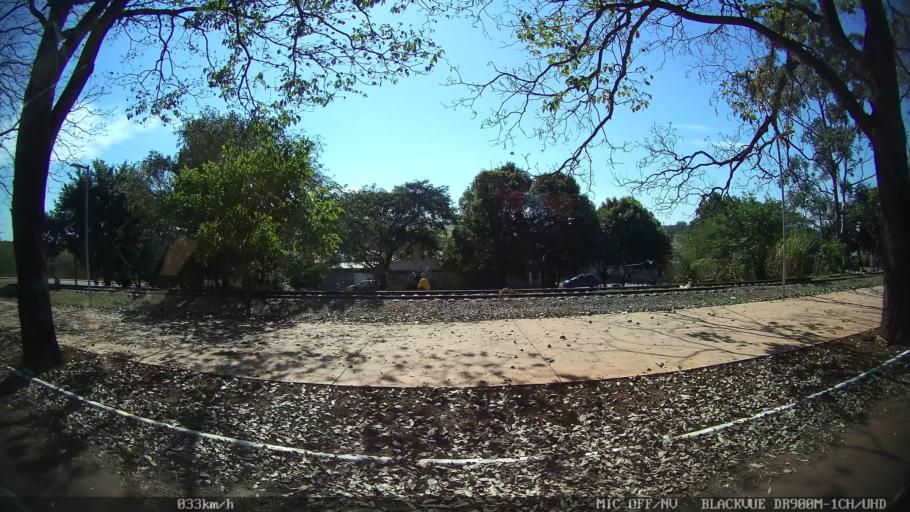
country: BR
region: Sao Paulo
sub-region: Santa Barbara D'Oeste
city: Santa Barbara d'Oeste
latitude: -22.7386
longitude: -47.4163
